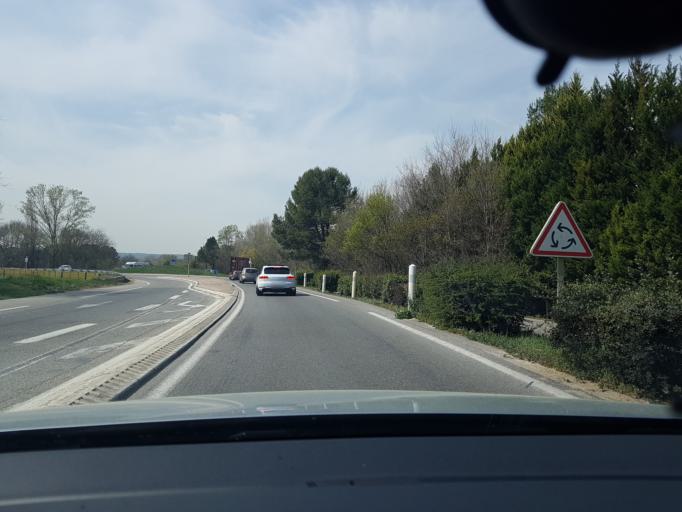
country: FR
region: Provence-Alpes-Cote d'Azur
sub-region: Departement des Bouches-du-Rhone
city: Chateauneuf-le-Rouge
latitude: 43.4781
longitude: 5.5703
